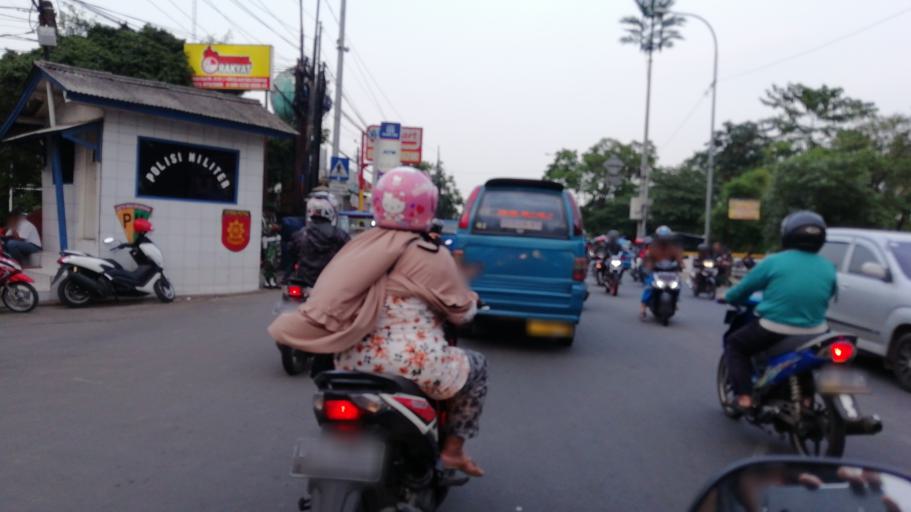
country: ID
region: West Java
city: Cibinong
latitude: -6.4361
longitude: 106.8528
